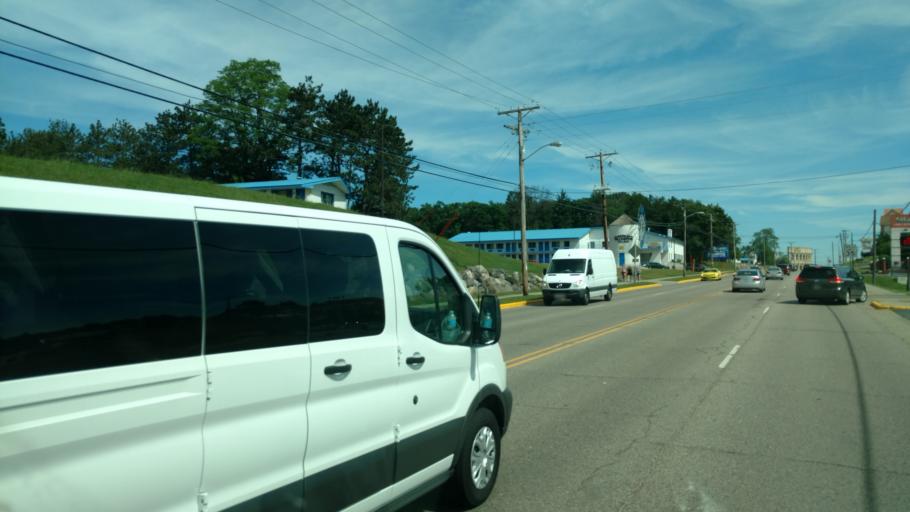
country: US
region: Wisconsin
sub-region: Sauk County
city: Lake Delton
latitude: 43.6067
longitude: -89.7914
